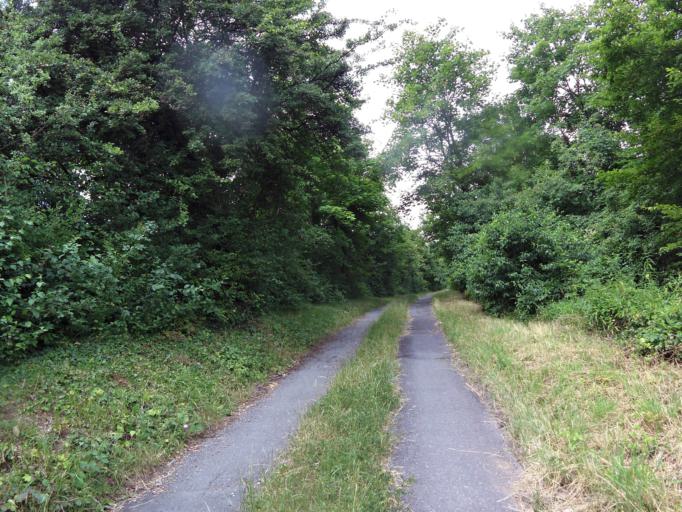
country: DE
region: Bavaria
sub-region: Regierungsbezirk Unterfranken
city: Wuerzburg
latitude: 49.7662
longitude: 9.9277
